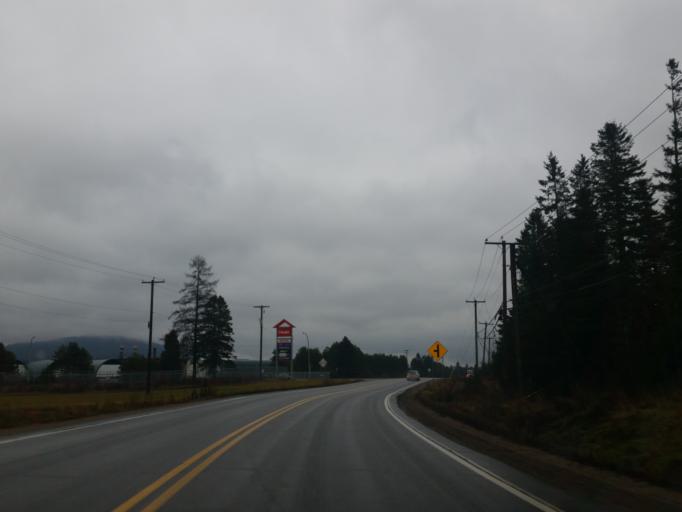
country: CA
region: Quebec
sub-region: Capitale-Nationale
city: Shannon
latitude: 46.8866
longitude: -71.5037
